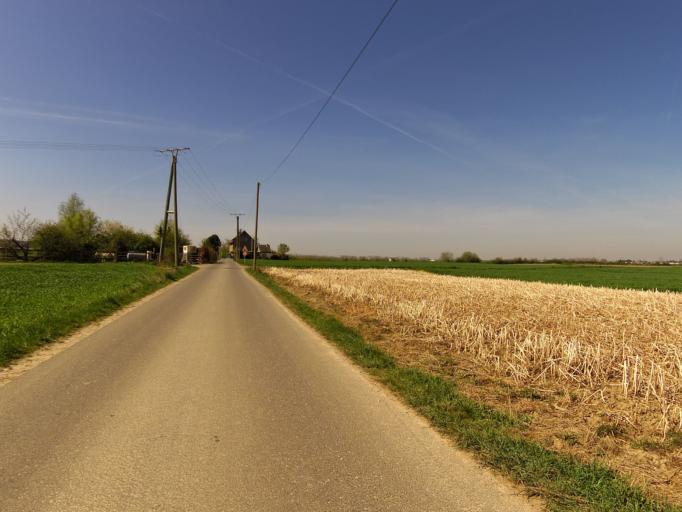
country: DE
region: North Rhine-Westphalia
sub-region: Regierungsbezirk Koln
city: Rheinbach
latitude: 50.6403
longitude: 6.9081
